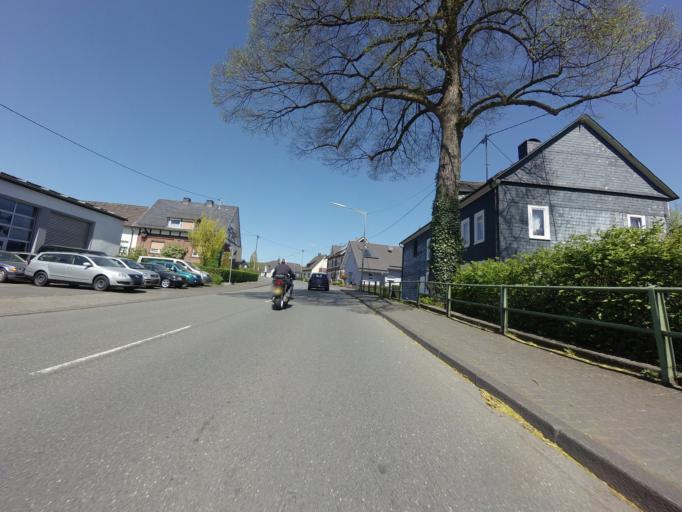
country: DE
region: North Rhine-Westphalia
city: Kreuztal
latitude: 50.9957
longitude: 7.9572
